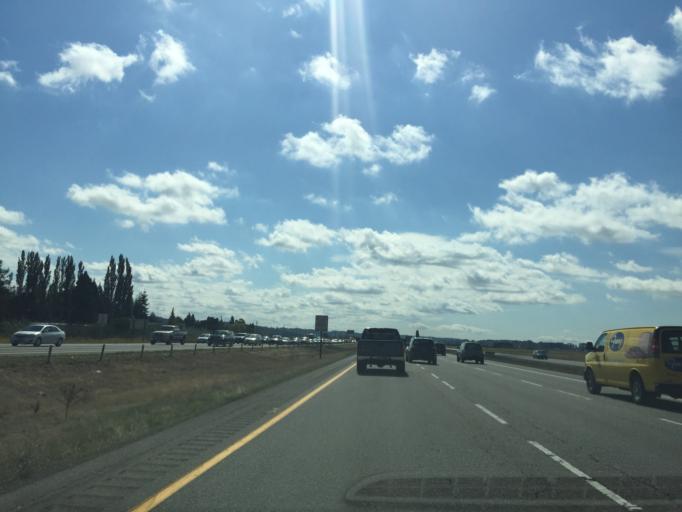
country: US
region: Washington
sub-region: Skagit County
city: Mount Vernon
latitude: 48.3718
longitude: -122.3359
